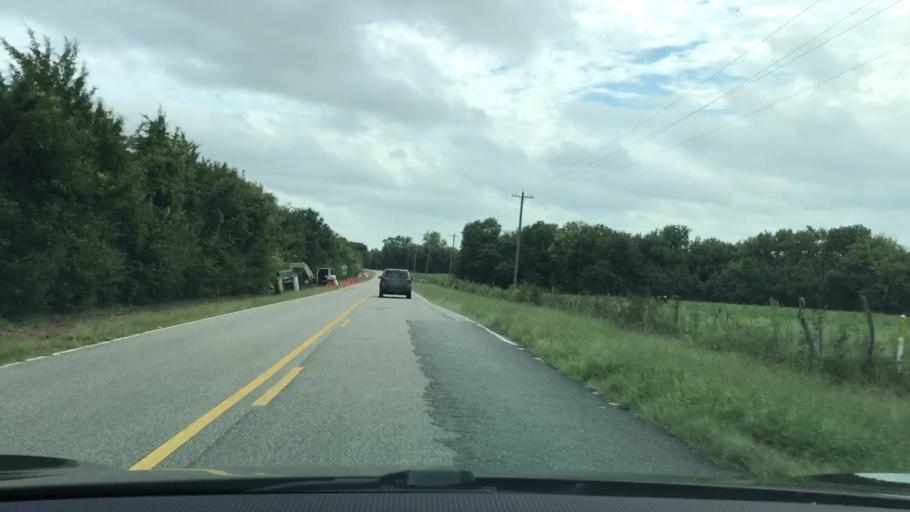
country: US
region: Alabama
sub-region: Montgomery County
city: Pike Road
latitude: 32.2902
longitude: -86.0760
